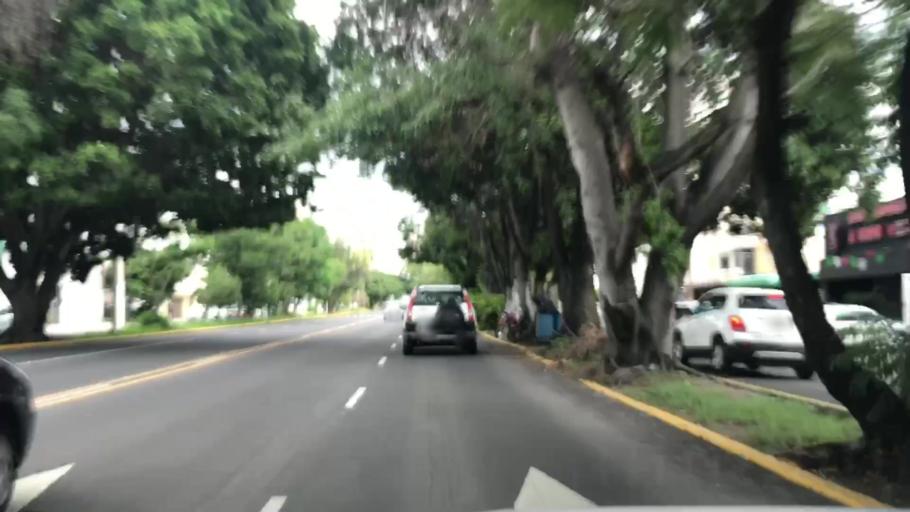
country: MX
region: Jalisco
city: Guadalajara
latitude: 20.6270
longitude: -103.4165
